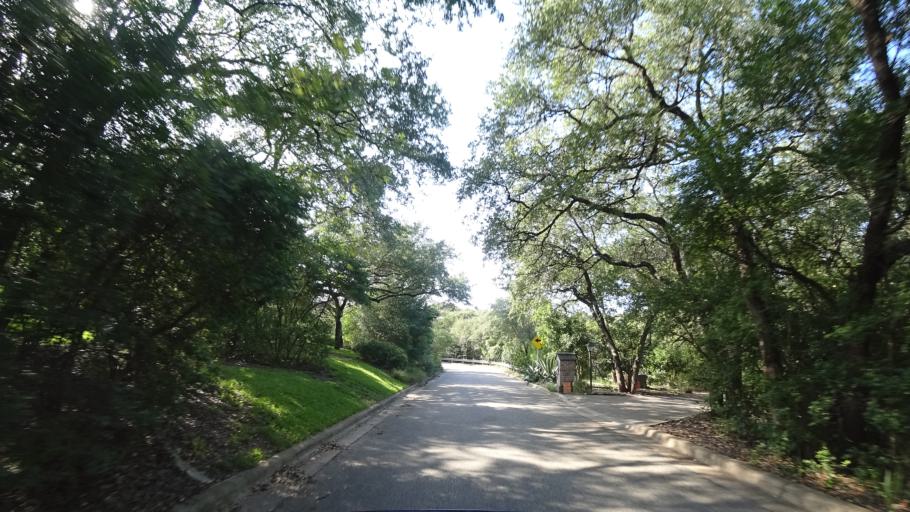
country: US
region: Texas
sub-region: Travis County
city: Rollingwood
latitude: 30.2840
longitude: -97.7974
